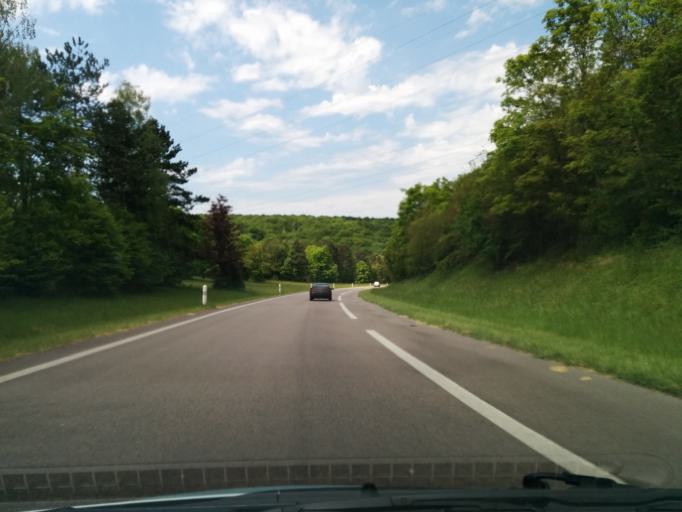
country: FR
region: Ile-de-France
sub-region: Departement des Yvelines
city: Bonnieres-sur-Seine
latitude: 49.0150
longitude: 1.5892
